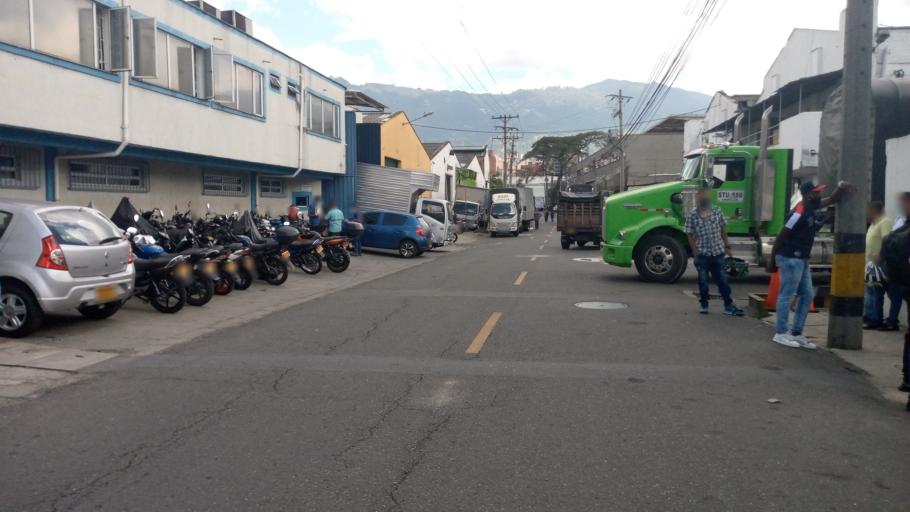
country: CO
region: Antioquia
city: Envigado
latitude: 6.1812
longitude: -75.5936
